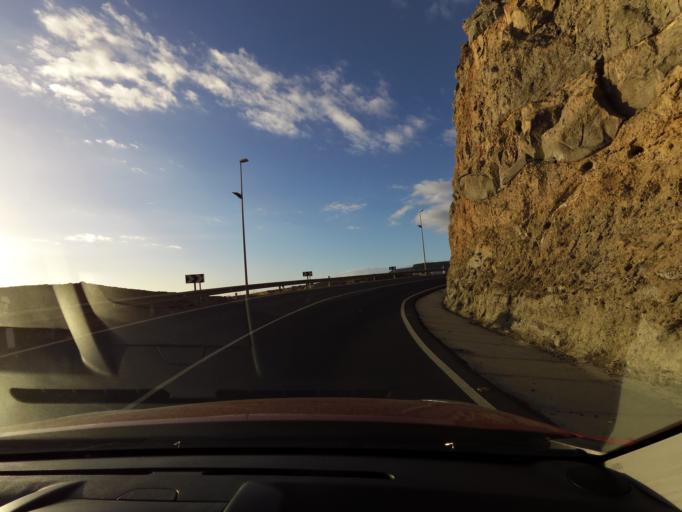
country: ES
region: Canary Islands
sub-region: Provincia de Las Palmas
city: Puerto Rico
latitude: 27.7875
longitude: -15.7225
